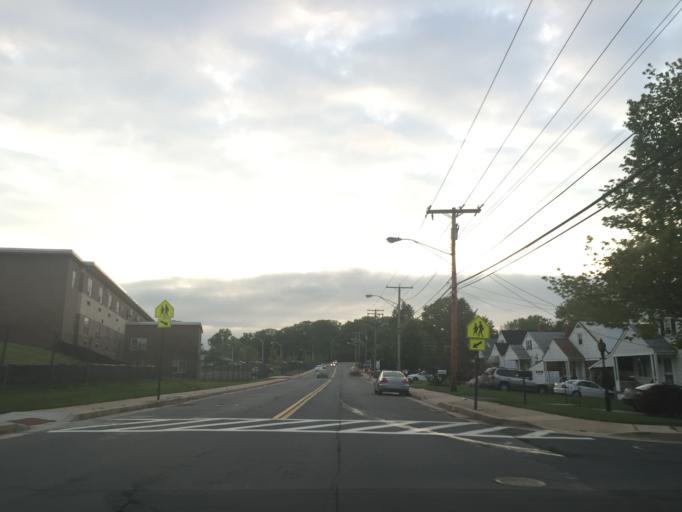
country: US
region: Maryland
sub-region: Baltimore County
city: Overlea
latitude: 39.3640
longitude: -76.5303
